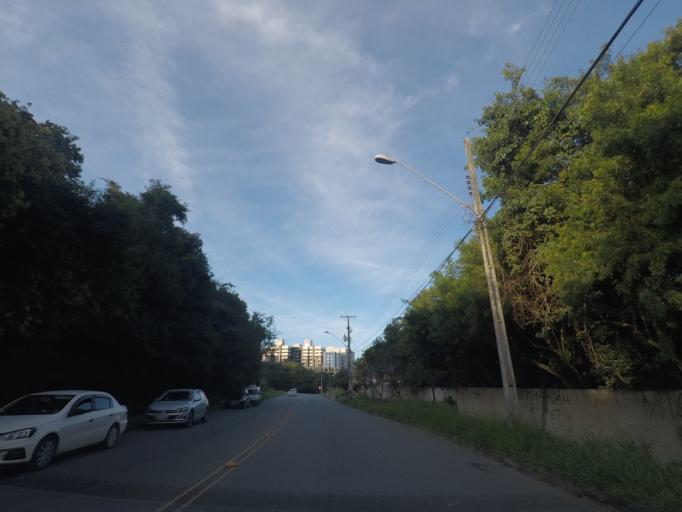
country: BR
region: Parana
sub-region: Curitiba
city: Curitiba
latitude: -25.4024
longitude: -49.2574
